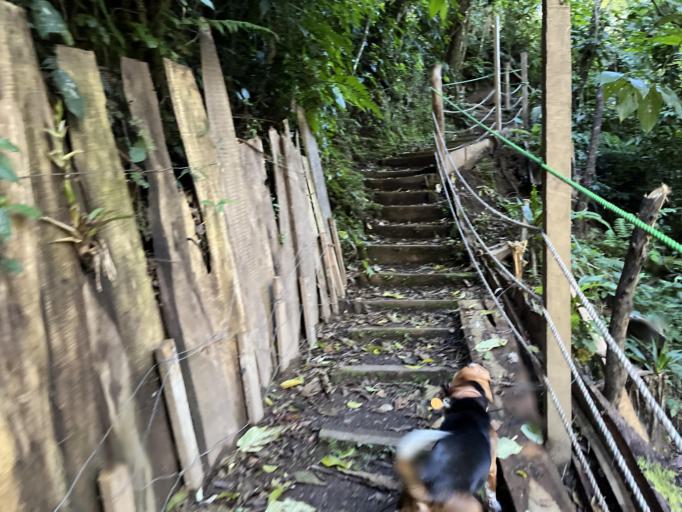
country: CR
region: Heredia
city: Angeles
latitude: 10.0399
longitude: -84.0425
